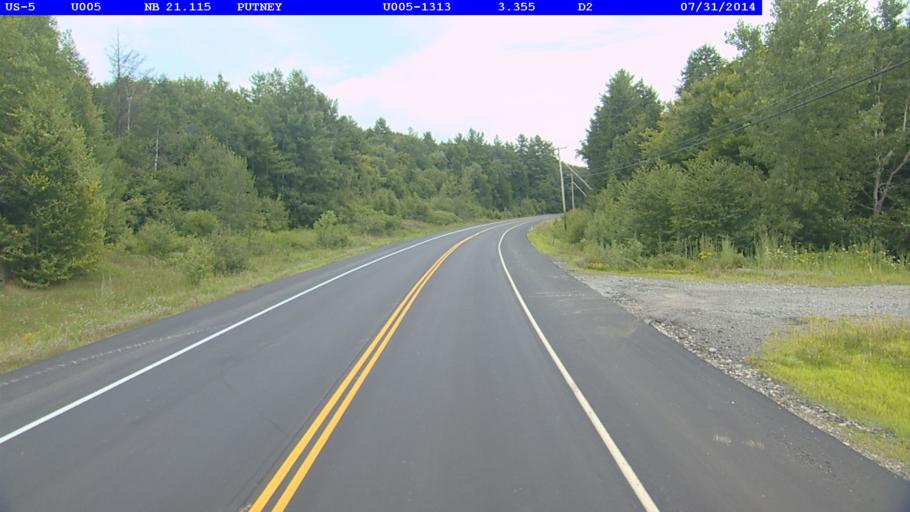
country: US
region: New Hampshire
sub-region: Cheshire County
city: Westmoreland
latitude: 42.9995
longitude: -72.4855
